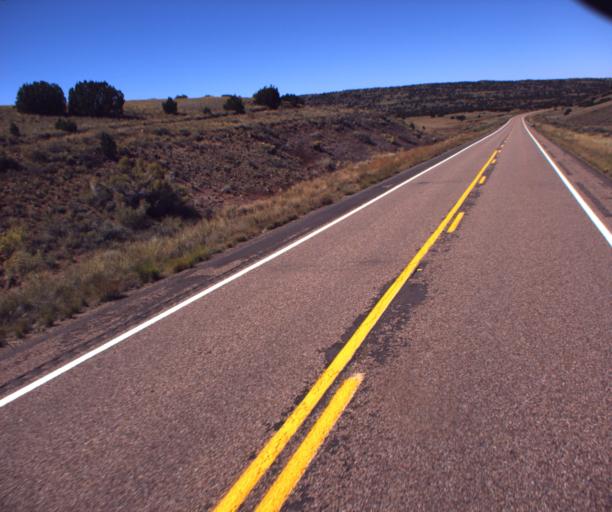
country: US
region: Arizona
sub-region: Apache County
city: Saint Johns
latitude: 34.5698
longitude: -109.5160
